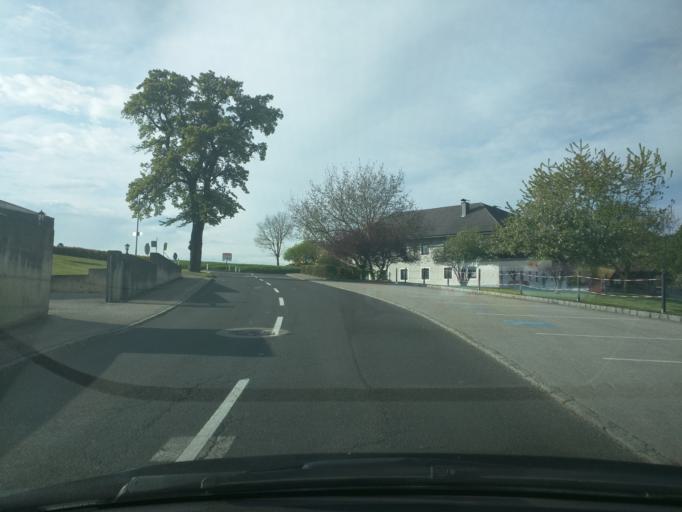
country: AT
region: Upper Austria
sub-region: Politischer Bezirk Kirchdorf an der Krems
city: Kremsmunster
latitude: 48.0998
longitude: 14.1106
